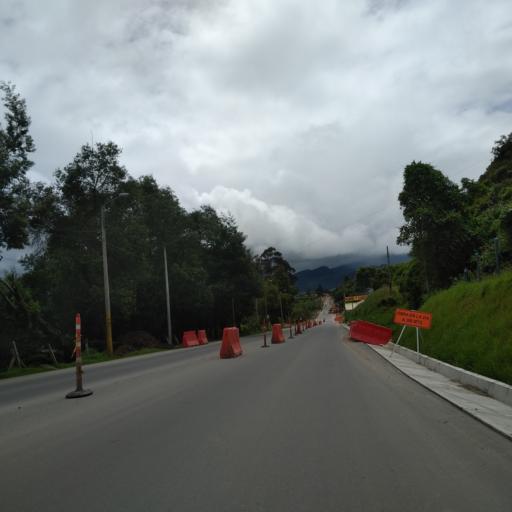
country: CO
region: Cundinamarca
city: La Calera
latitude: 4.7001
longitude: -73.9823
